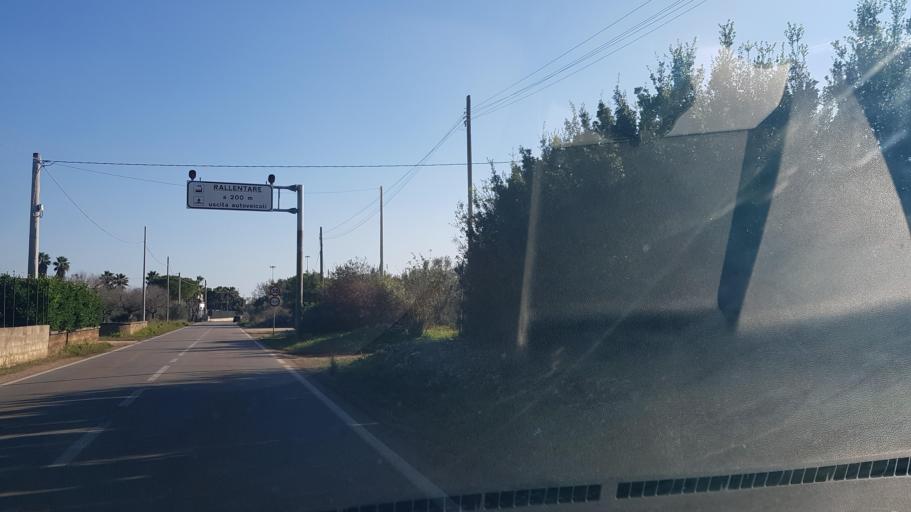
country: IT
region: Apulia
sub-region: Provincia di Lecce
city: Montesano Salentino
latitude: 39.9600
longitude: 18.3366
